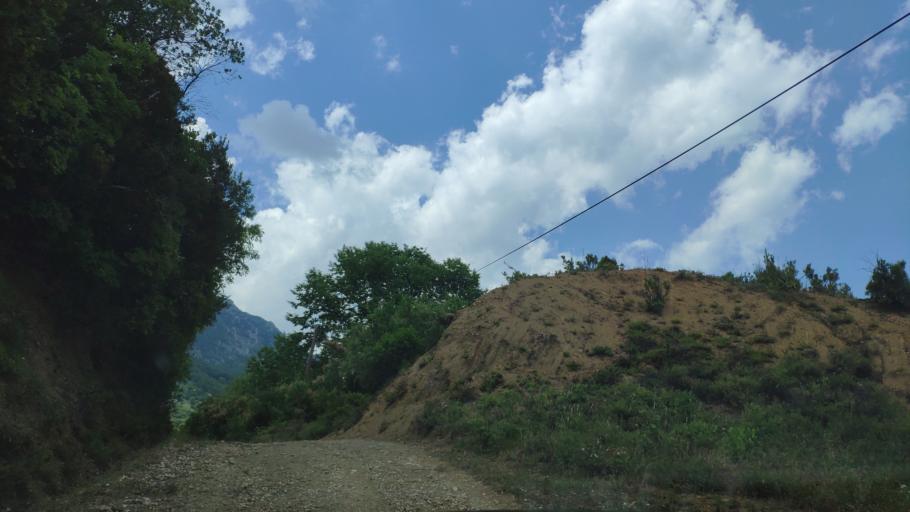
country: GR
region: Epirus
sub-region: Nomos Artas
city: Agios Dimitrios
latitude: 39.3197
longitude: 21.0089
